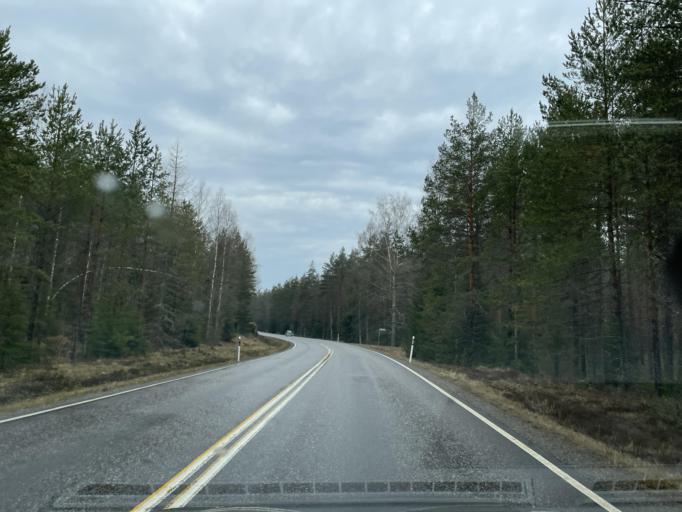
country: FI
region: Paijanne Tavastia
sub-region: Lahti
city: Auttoinen
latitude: 61.2321
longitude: 25.1067
